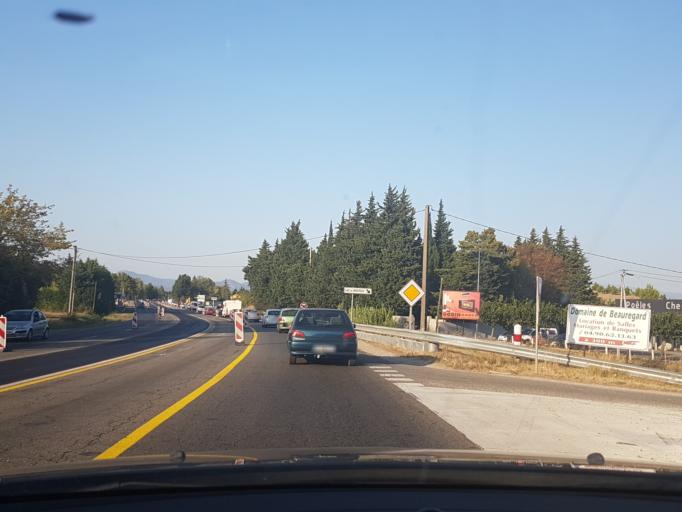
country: FR
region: Provence-Alpes-Cote d'Azur
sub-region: Departement du Vaucluse
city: Althen-des-Paluds
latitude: 44.0156
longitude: 4.9595
